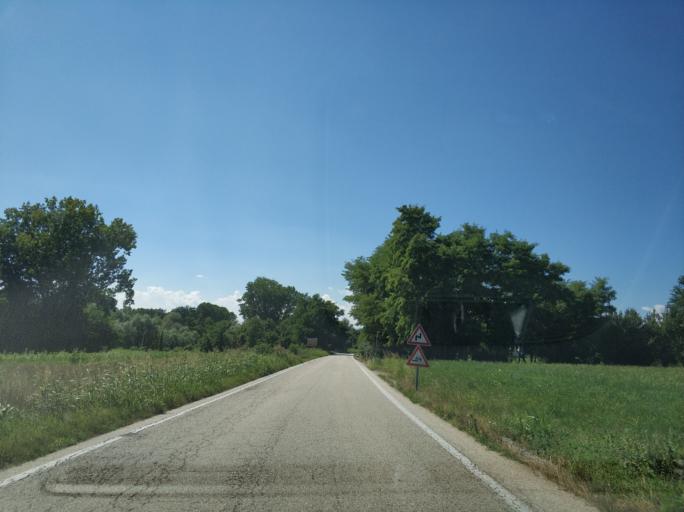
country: IT
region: Piedmont
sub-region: Provincia di Torino
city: San Benigno Canavese
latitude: 45.2171
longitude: 7.7954
